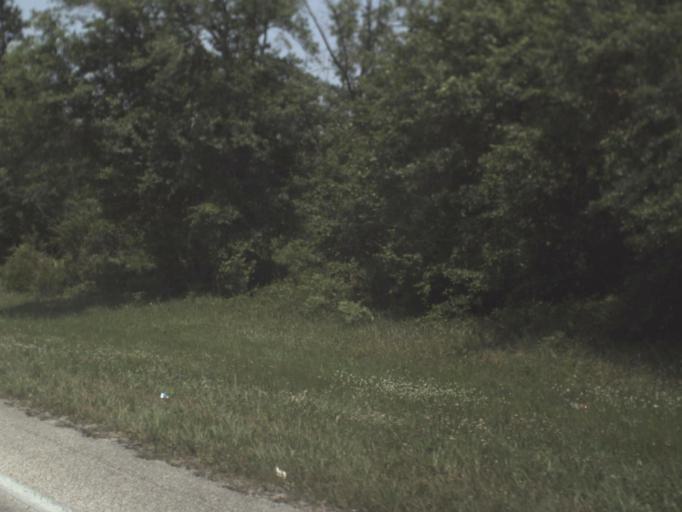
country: US
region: Florida
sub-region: Bradford County
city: Starke
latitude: 30.1021
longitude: -82.0529
